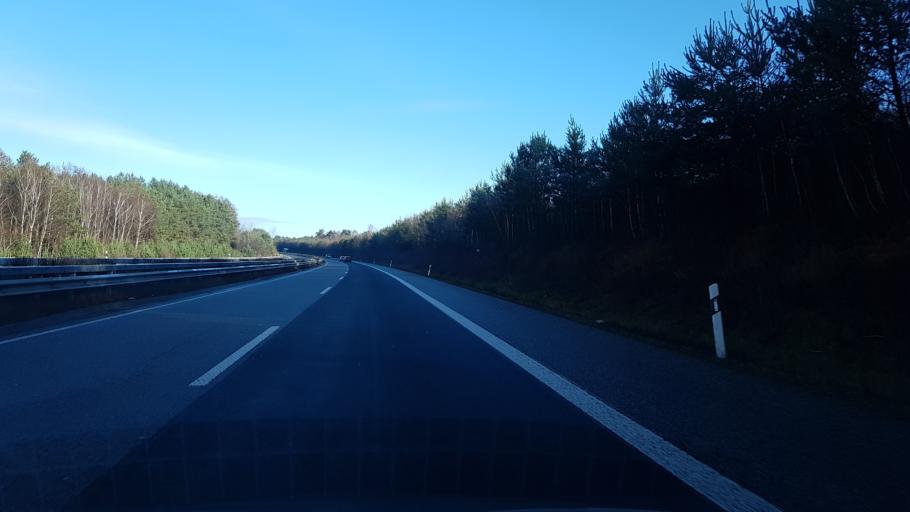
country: DE
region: Rheinland-Pfalz
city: Mehlingen
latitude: 49.4786
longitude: 7.8344
